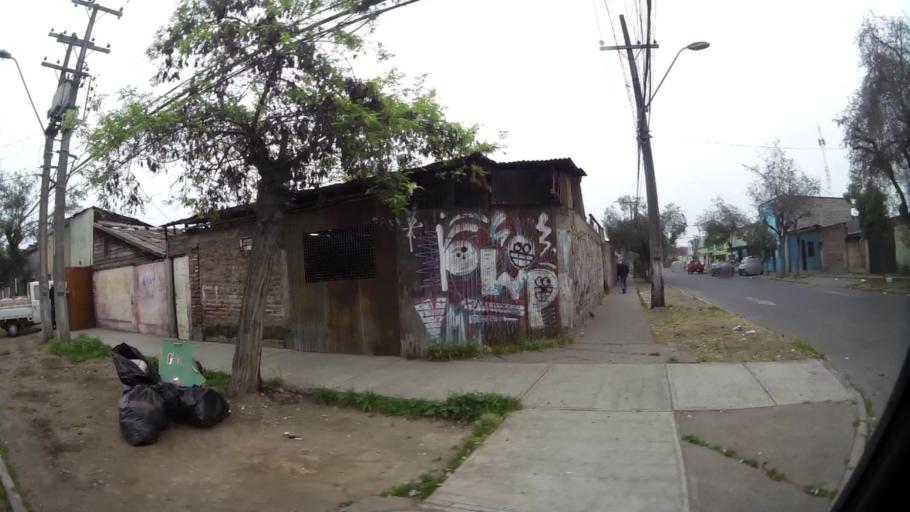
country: CL
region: Santiago Metropolitan
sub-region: Provincia de Santiago
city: Santiago
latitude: -33.4919
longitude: -70.6359
